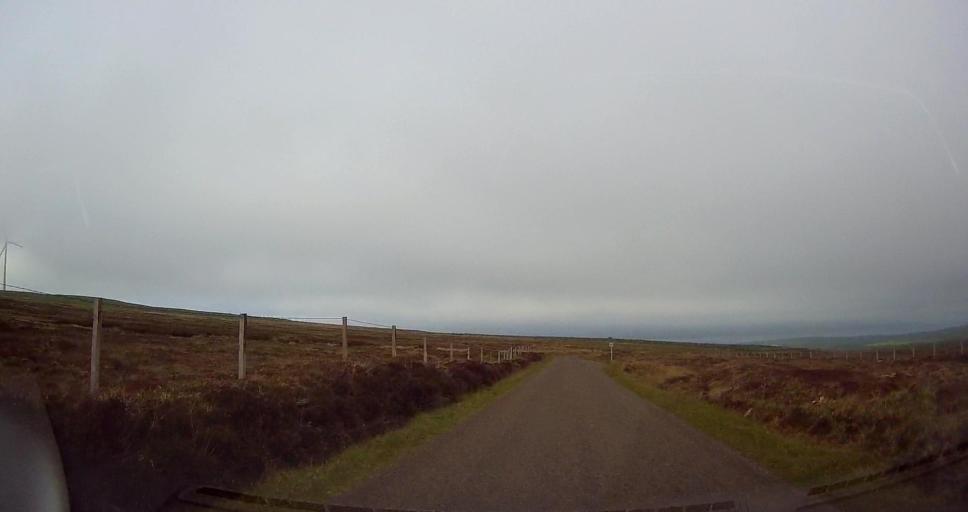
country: GB
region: Scotland
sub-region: Orkney Islands
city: Stromness
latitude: 59.1030
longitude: -3.1354
